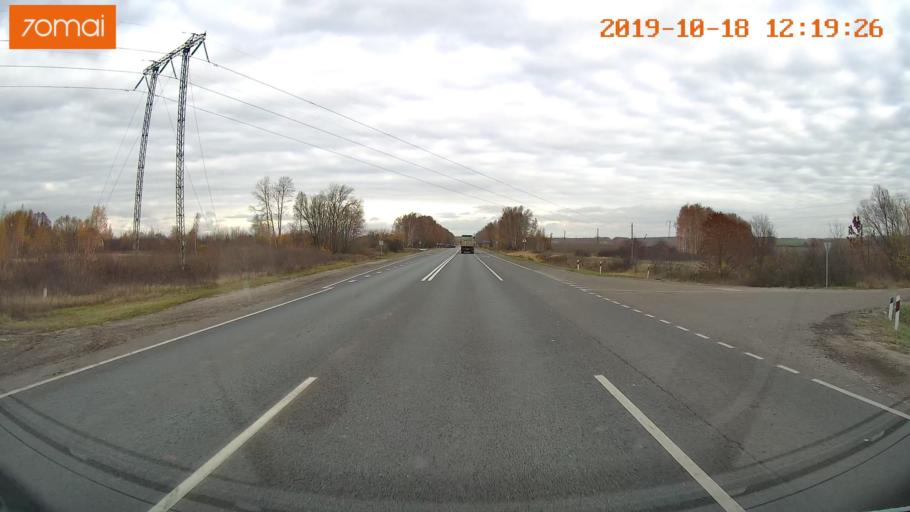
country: RU
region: Rjazan
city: Zakharovo
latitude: 54.4823
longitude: 39.4681
